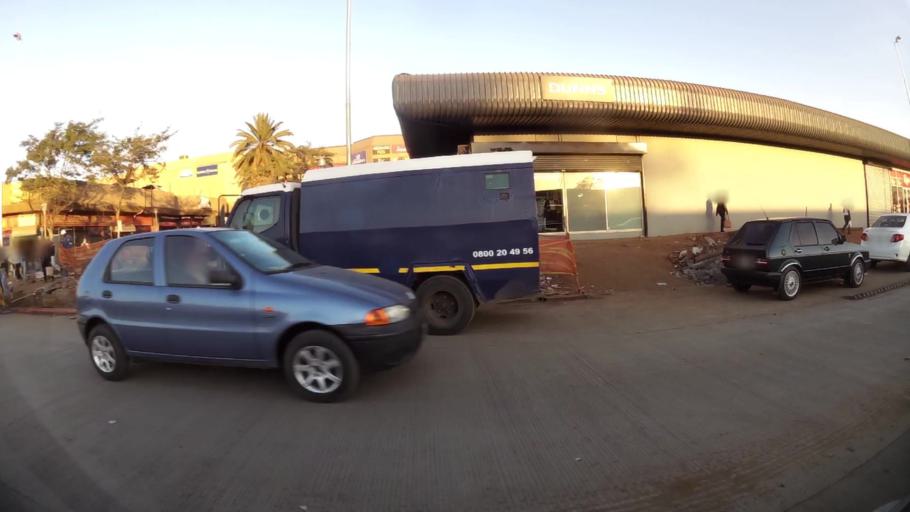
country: ZA
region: North-West
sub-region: Bojanala Platinum District Municipality
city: Rustenburg
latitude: -25.6670
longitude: 27.2406
